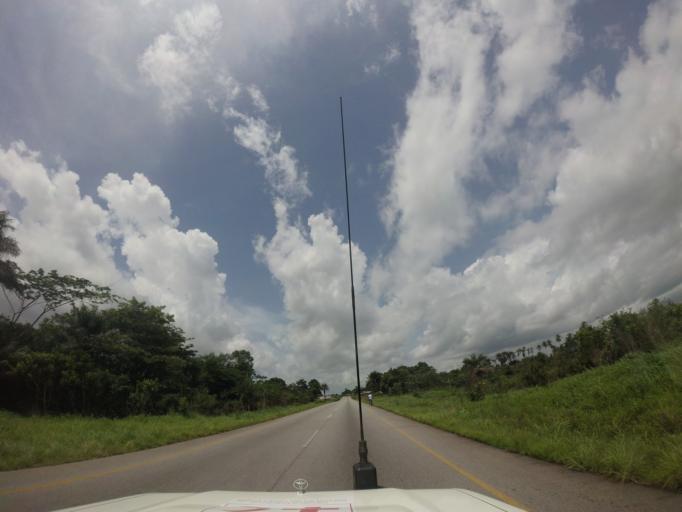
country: SL
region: Northern Province
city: Lunsar
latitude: 8.4853
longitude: -12.6192
